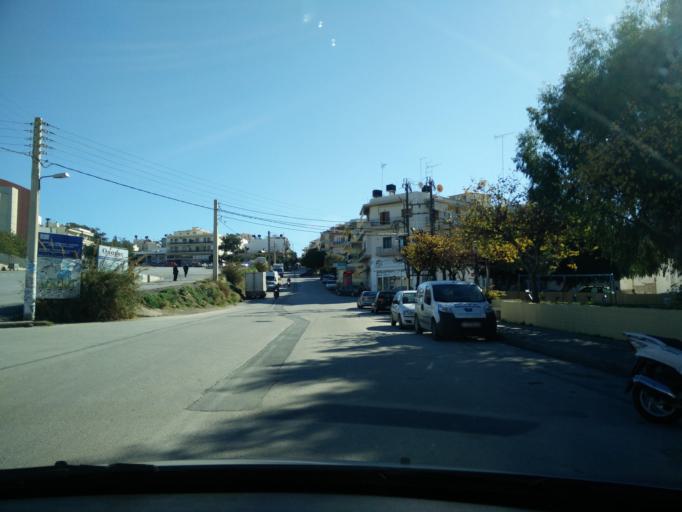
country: GR
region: Crete
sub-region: Nomos Irakleiou
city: Irakleion
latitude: 35.3308
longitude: 25.1402
